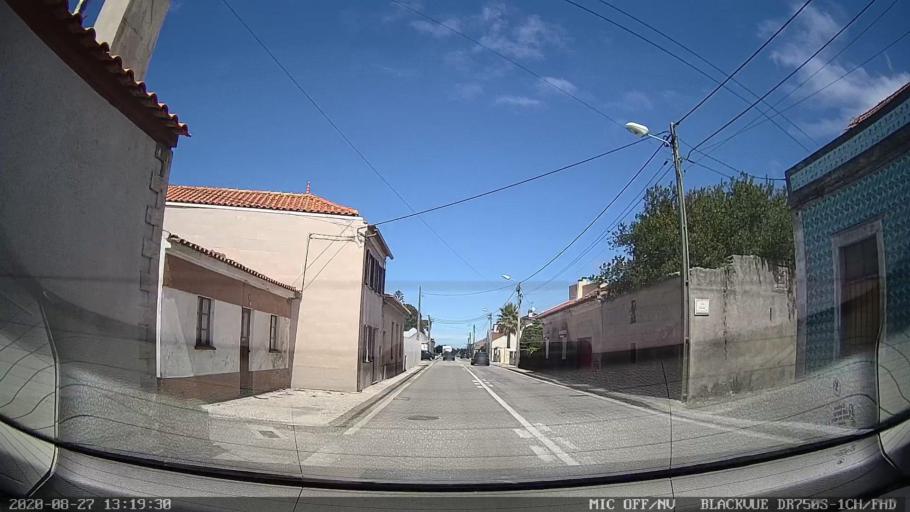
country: PT
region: Aveiro
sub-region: Vagos
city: Vagos
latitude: 40.5631
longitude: -8.6825
